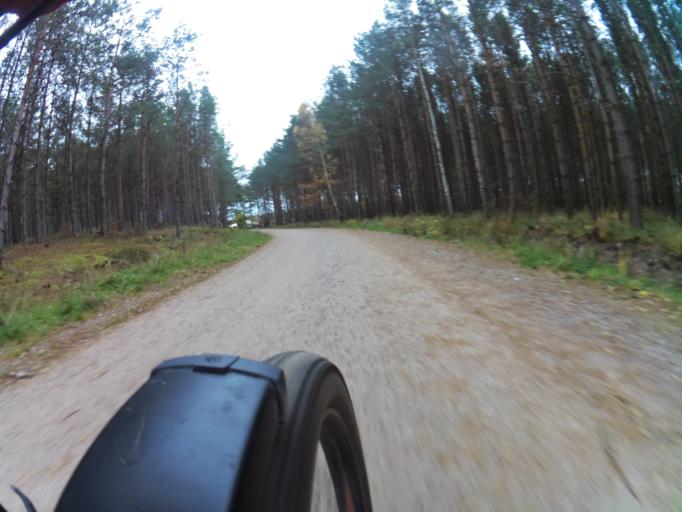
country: PL
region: Pomeranian Voivodeship
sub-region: Powiat wejherowski
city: Choczewo
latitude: 54.7815
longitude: 17.7353
